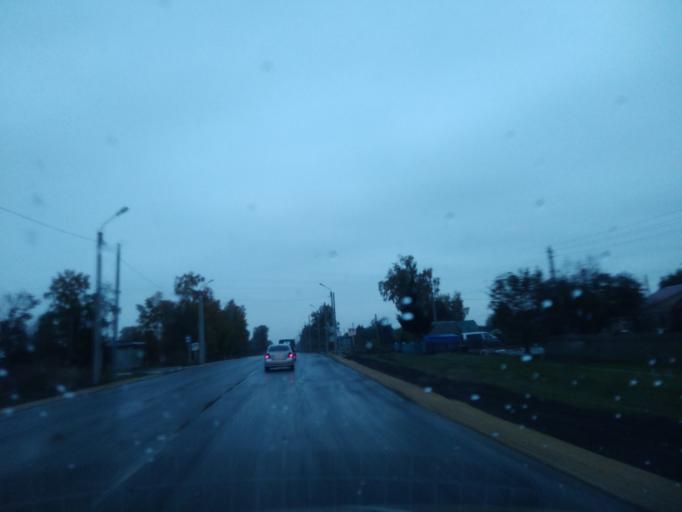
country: RU
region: Tula
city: Teploye
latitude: 53.5823
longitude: 37.6390
